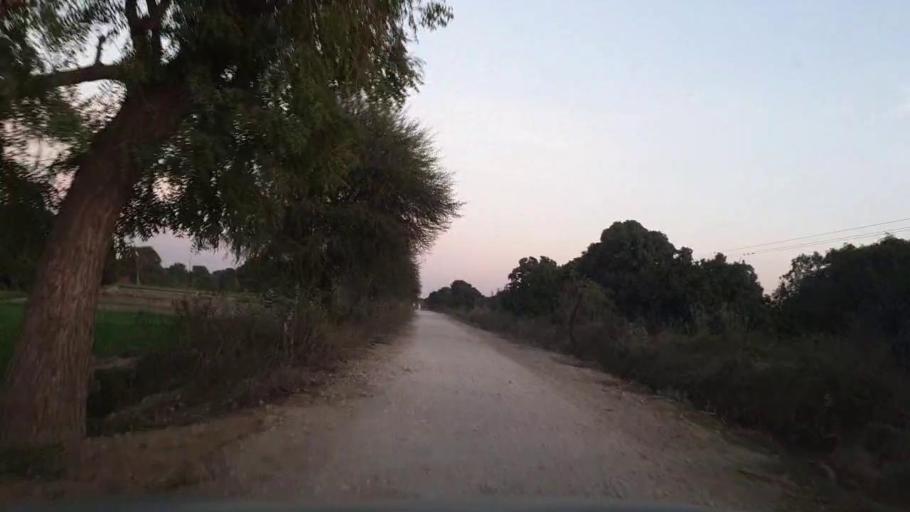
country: PK
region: Sindh
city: Tando Allahyar
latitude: 25.5556
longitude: 68.7860
